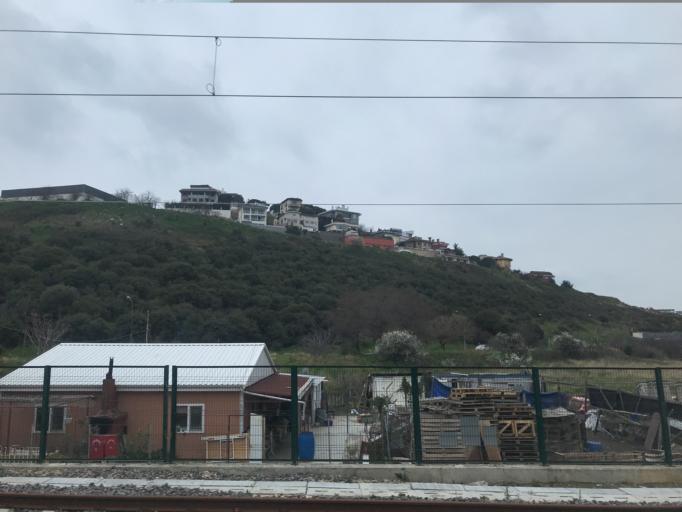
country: TR
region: Istanbul
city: Maltepe
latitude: 40.9149
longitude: 29.1468
